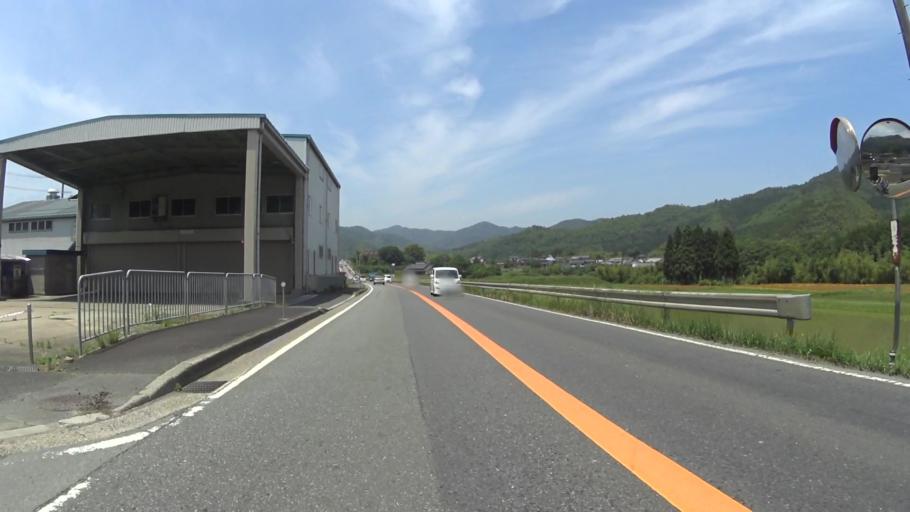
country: JP
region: Kyoto
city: Ayabe
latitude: 35.2435
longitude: 135.2170
